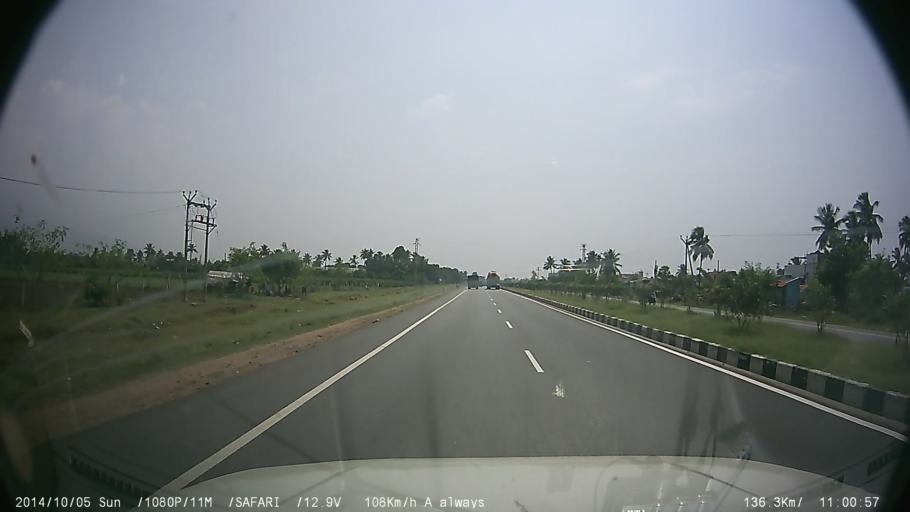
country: IN
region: Tamil Nadu
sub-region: Salem
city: Attur
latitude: 11.6189
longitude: 78.5539
